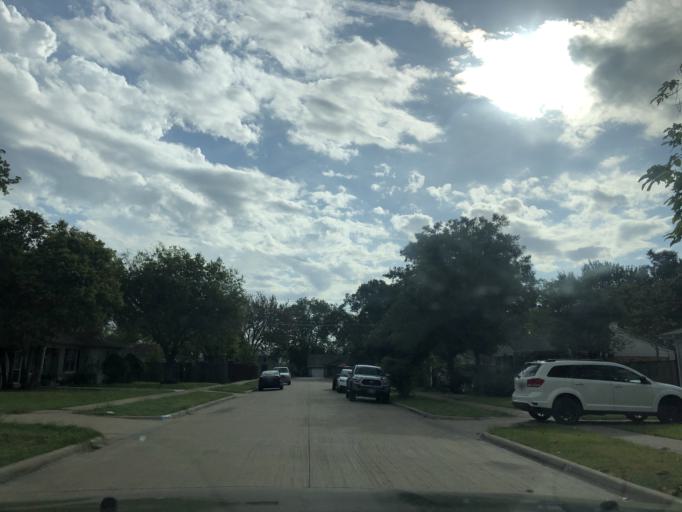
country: US
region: Texas
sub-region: Dallas County
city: Garland
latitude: 32.8797
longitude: -96.6629
